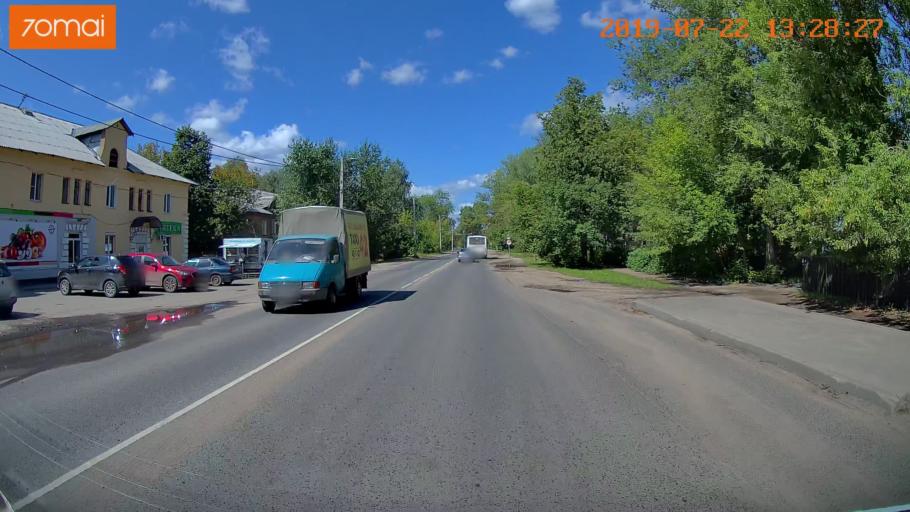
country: RU
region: Ivanovo
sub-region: Gorod Ivanovo
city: Ivanovo
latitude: 57.0420
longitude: 40.9475
